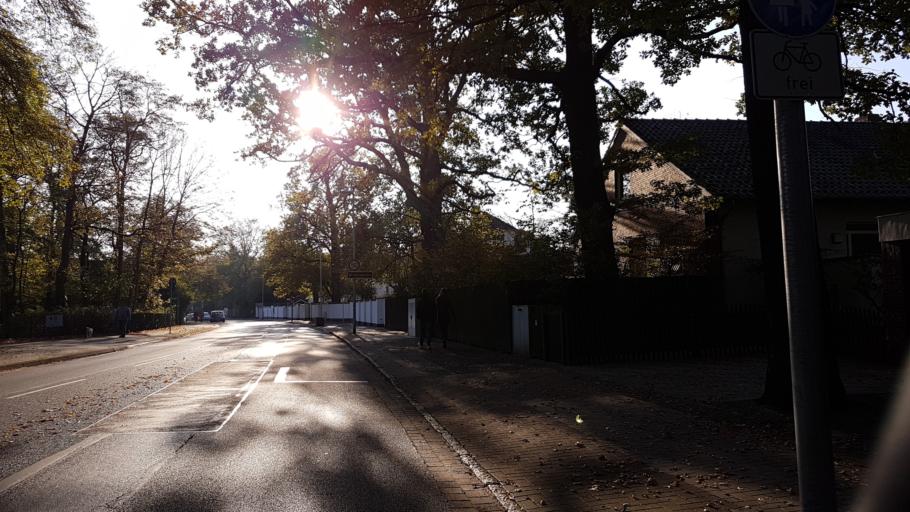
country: DE
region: Lower Saxony
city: Hannover
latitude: 52.3941
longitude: 9.7871
